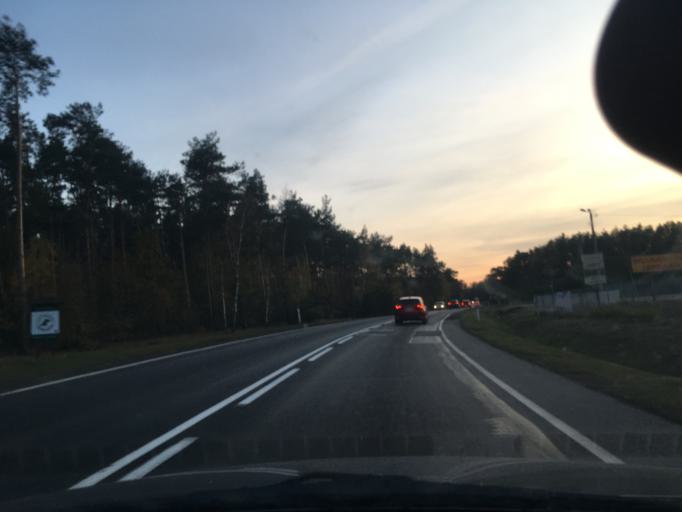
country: PL
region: Masovian Voivodeship
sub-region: Powiat sochaczewski
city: Mlodzieszyn
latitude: 52.3311
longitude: 20.2167
